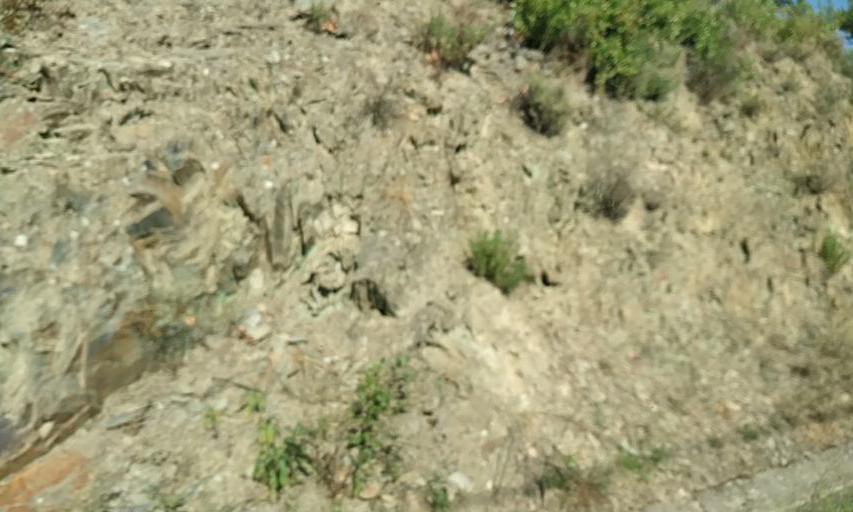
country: PT
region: Viseu
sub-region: Sao Joao da Pesqueira
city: Sao Joao da Pesqueira
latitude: 41.1834
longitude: -7.4401
